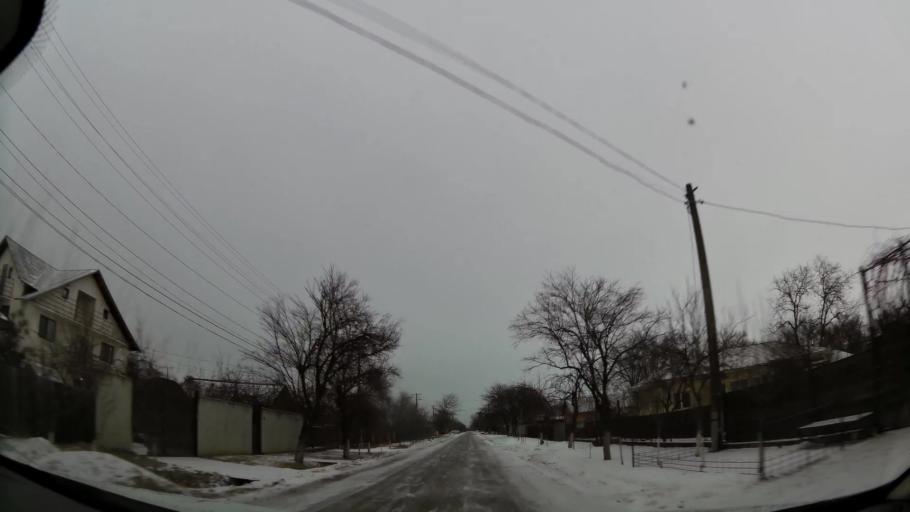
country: RO
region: Prahova
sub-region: Comuna Poenarii-Burchi
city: Ologeni
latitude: 44.7325
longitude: 25.9184
